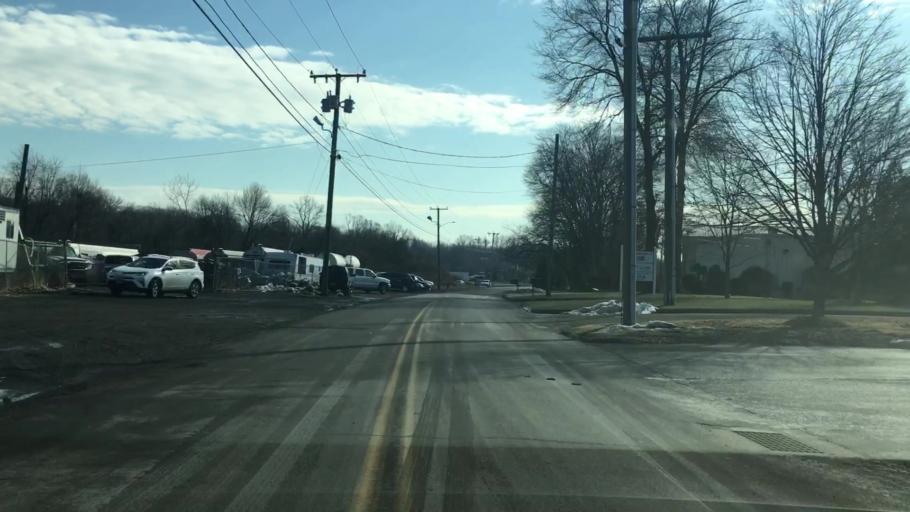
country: US
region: Connecticut
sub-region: Hartford County
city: Kensington
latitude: 41.6160
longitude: -72.7102
